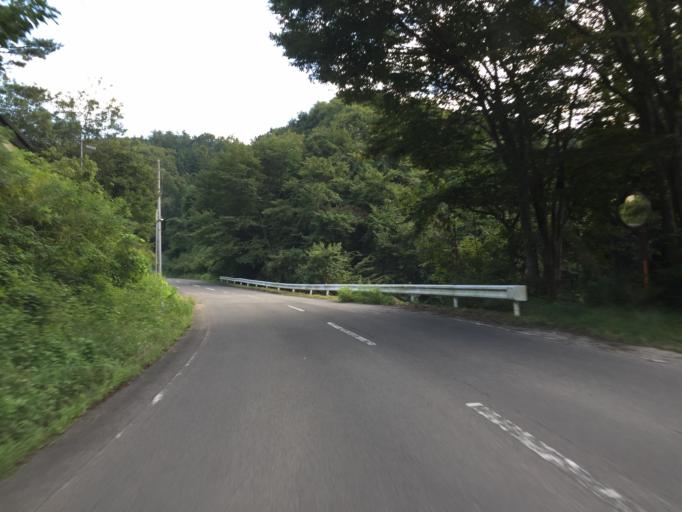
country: JP
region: Fukushima
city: Fukushima-shi
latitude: 37.6657
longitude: 140.5714
